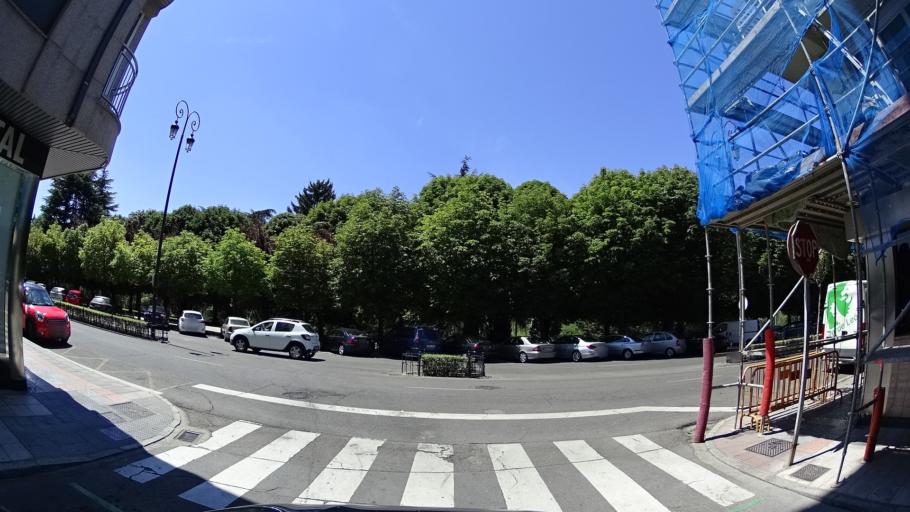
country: ES
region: Castille and Leon
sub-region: Provincia de Leon
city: Leon
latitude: 42.6005
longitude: -5.5812
